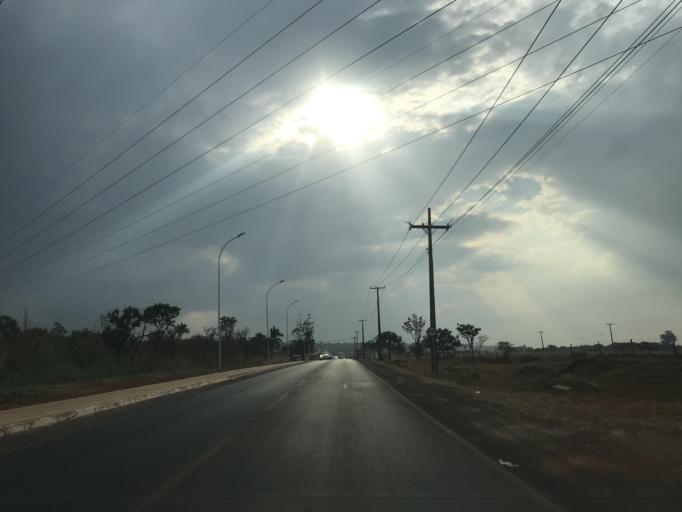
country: BR
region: Federal District
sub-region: Brasilia
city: Brasilia
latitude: -15.6632
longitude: -47.8283
